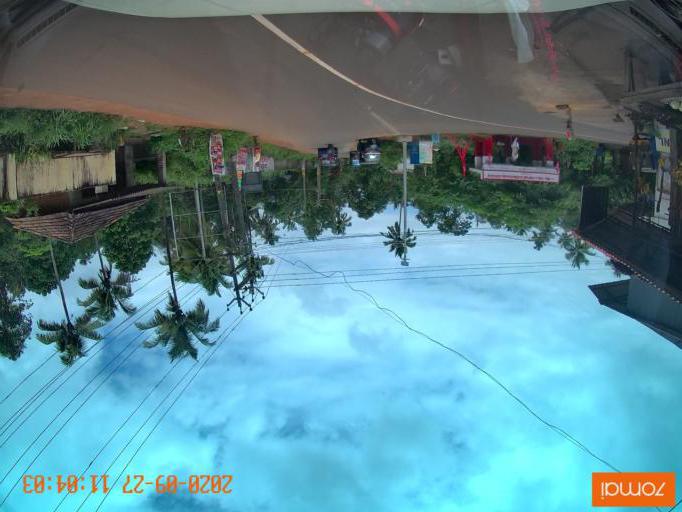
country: IN
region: Kerala
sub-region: Thrissur District
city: Irinjalakuda
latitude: 10.4223
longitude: 76.2521
